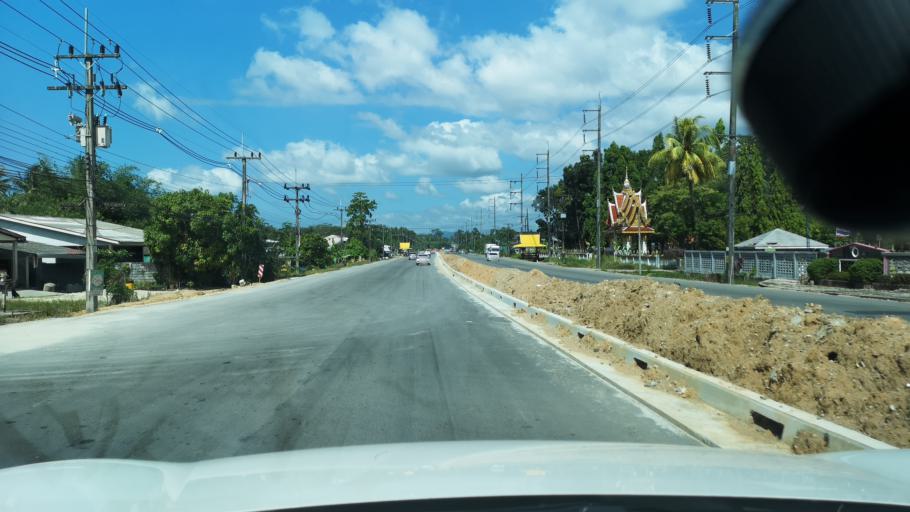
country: TH
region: Phangnga
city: Thai Mueang
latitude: 8.4415
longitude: 98.2569
